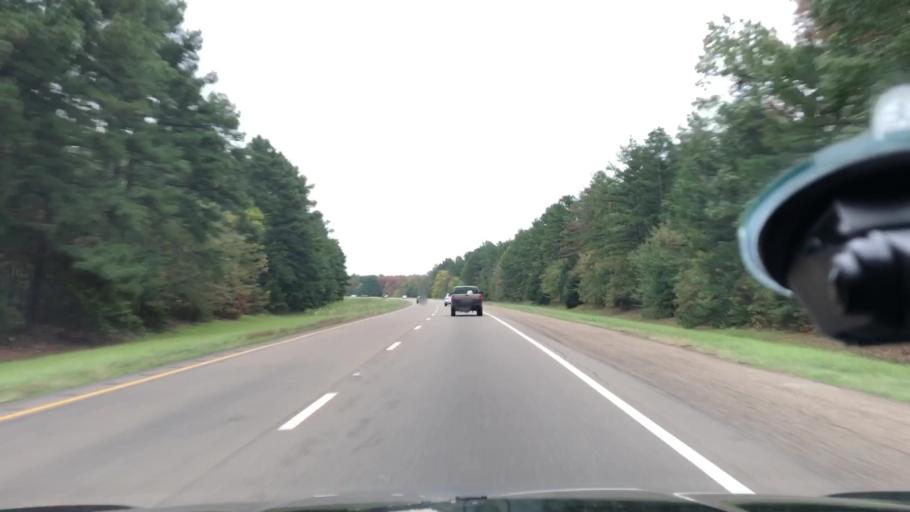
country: US
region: Texas
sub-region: Morris County
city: Naples
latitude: 33.2990
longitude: -94.7116
